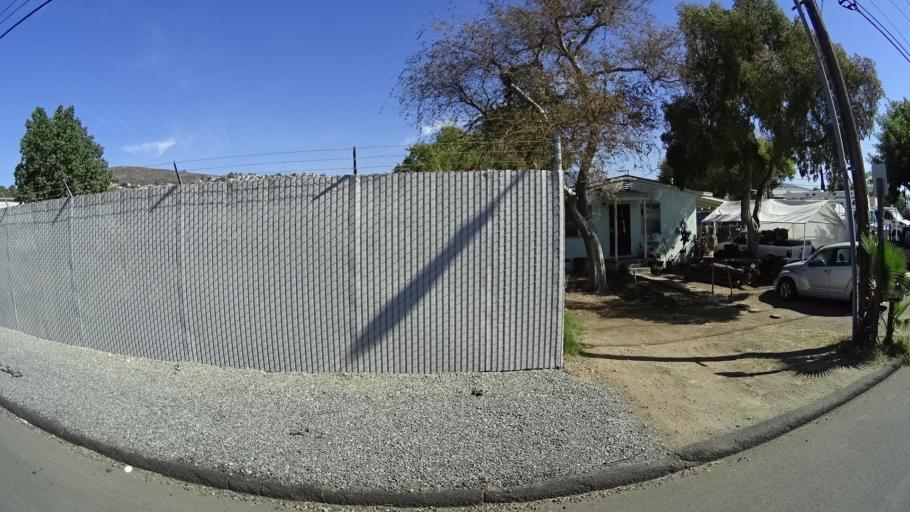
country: US
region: California
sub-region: San Diego County
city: La Presa
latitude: 32.7171
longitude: -117.0057
